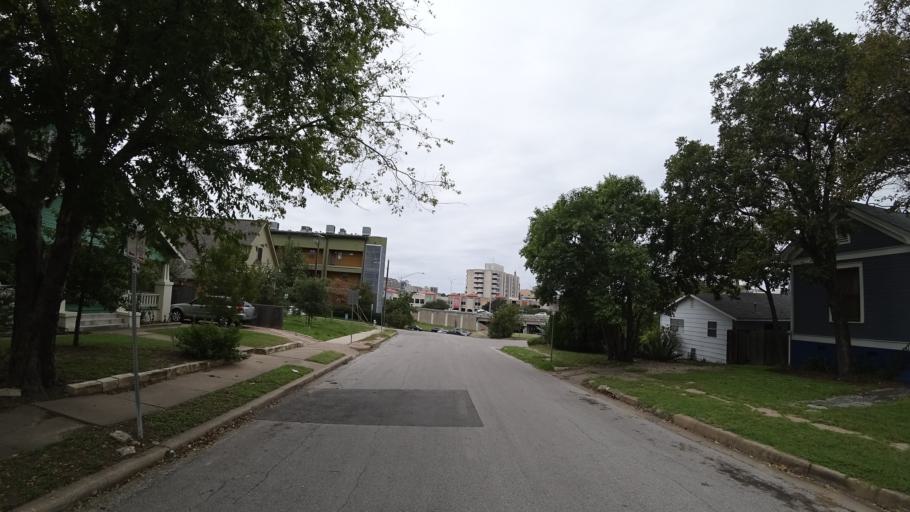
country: US
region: Texas
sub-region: Travis County
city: Austin
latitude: 30.2743
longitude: -97.7302
